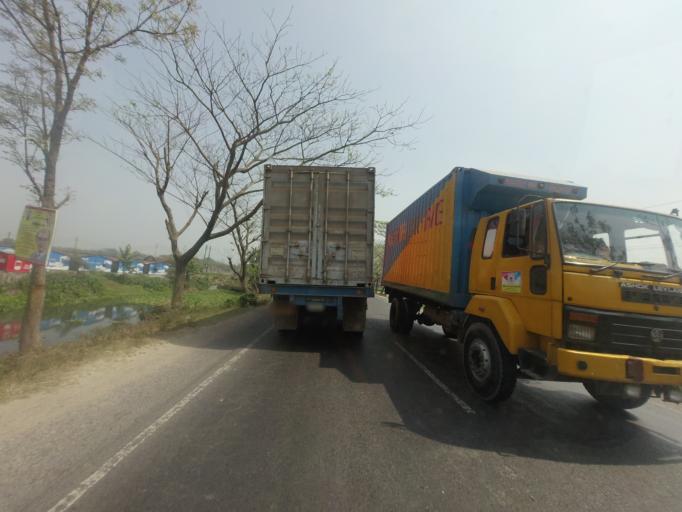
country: BD
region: Dhaka
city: Bhairab Bazar
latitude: 24.0488
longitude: 91.1008
